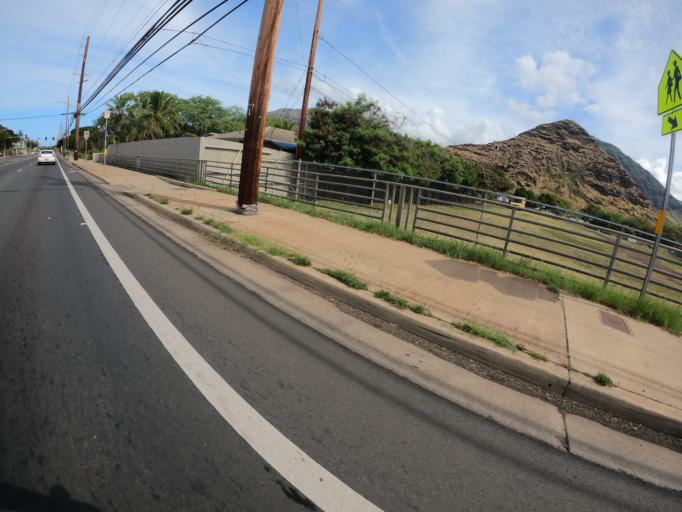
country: US
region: Hawaii
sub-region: Honolulu County
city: Makaha
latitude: 21.4565
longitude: -158.1985
